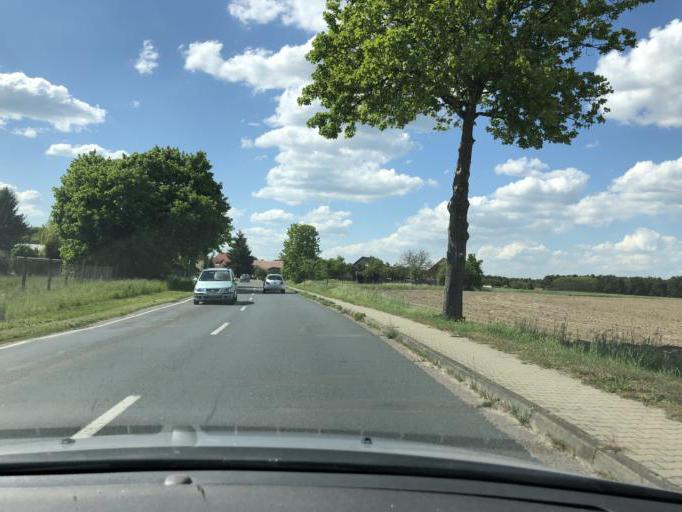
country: DE
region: Brandenburg
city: Spreenhagen
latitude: 52.3413
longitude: 13.8862
